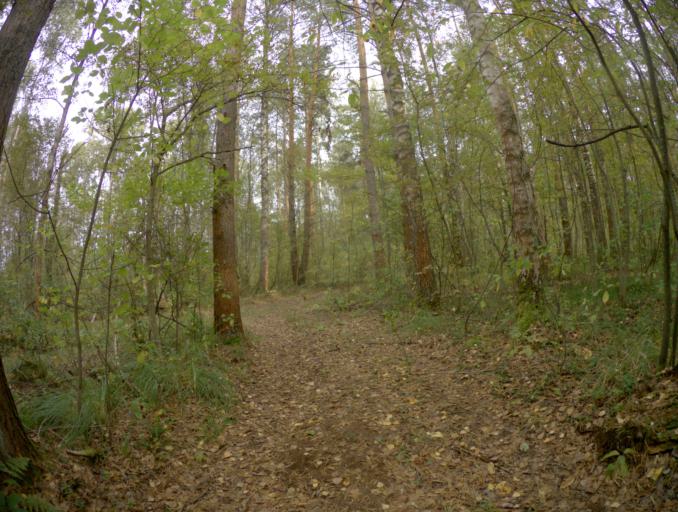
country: RU
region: Vladimir
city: Kommunar
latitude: 56.1325
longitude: 40.5028
